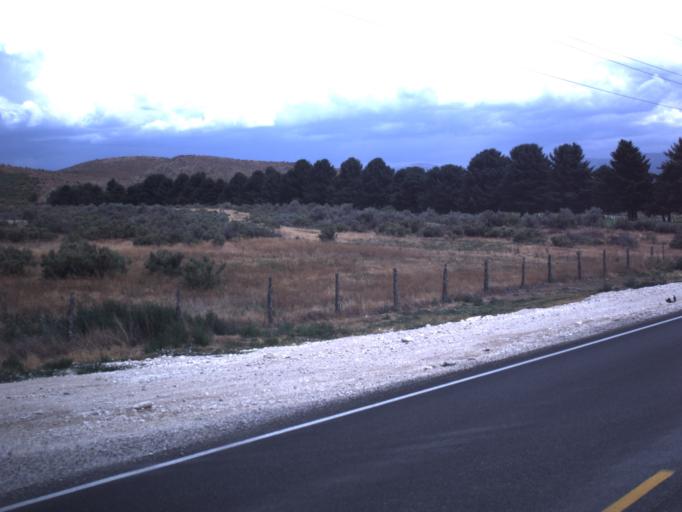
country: US
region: Utah
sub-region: Sanpete County
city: Moroni
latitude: 39.5432
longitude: -111.5964
